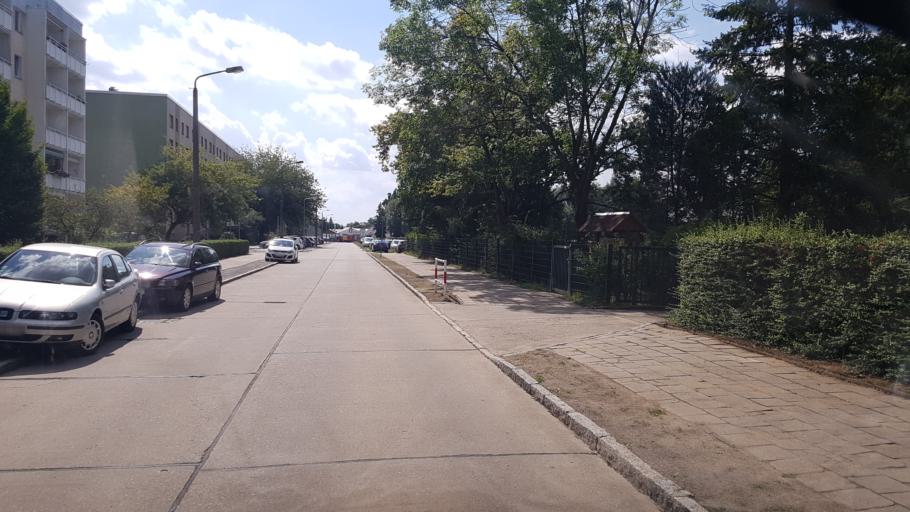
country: DE
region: Brandenburg
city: Lubbenau
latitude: 51.8630
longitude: 13.9371
